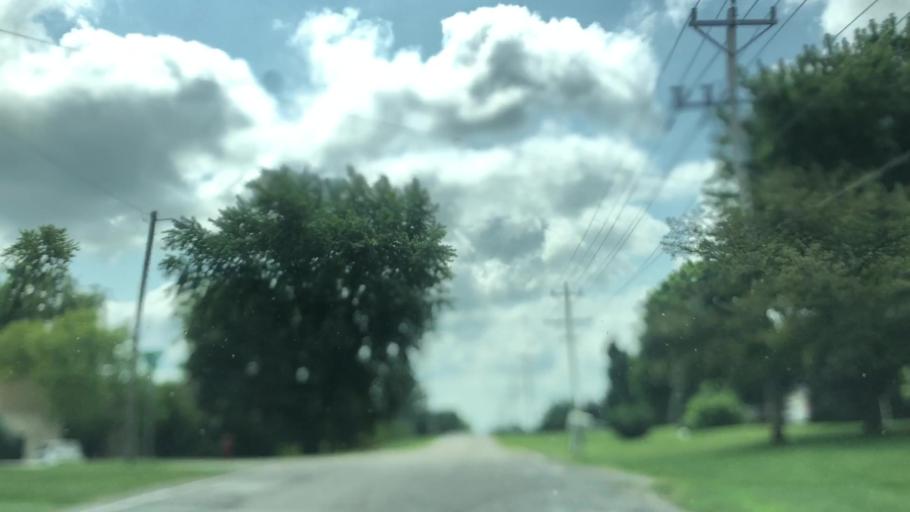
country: US
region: Iowa
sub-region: Marshall County
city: Marshalltown
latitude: 42.0415
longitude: -92.9611
